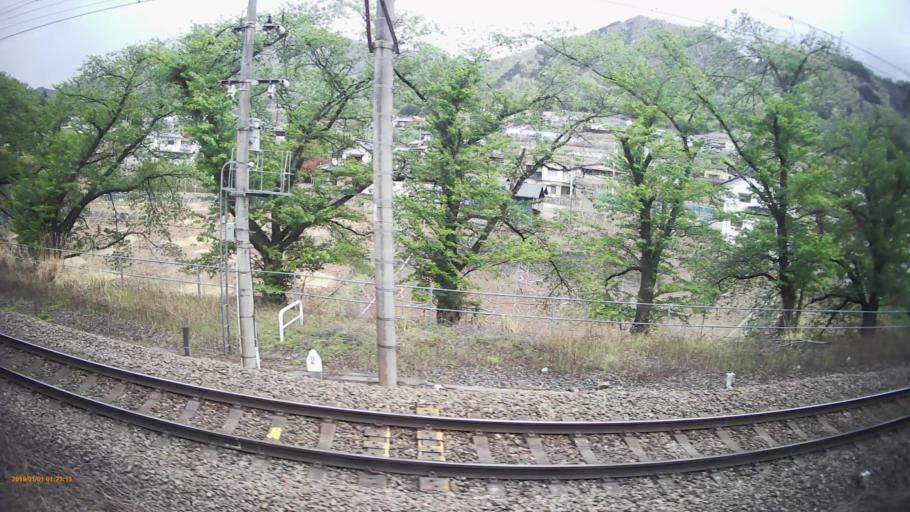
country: JP
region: Yamanashi
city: Enzan
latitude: 35.6743
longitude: 138.7434
